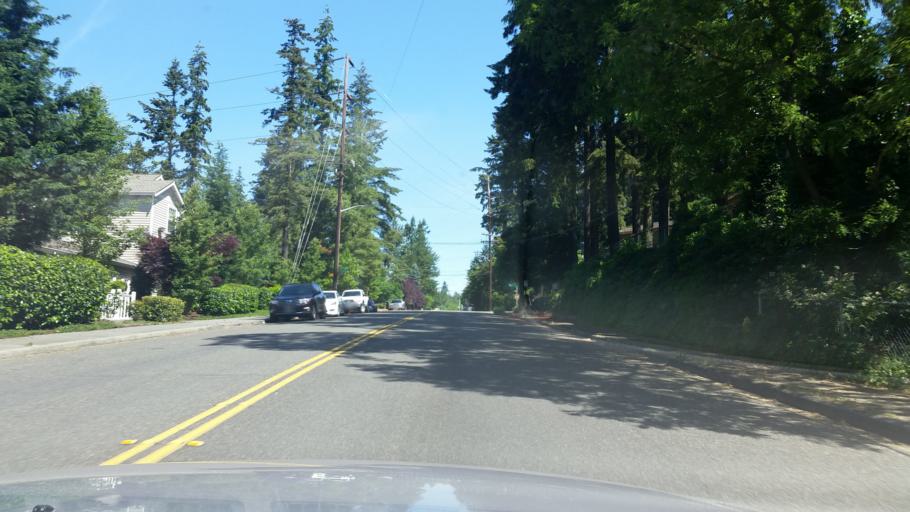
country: US
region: Washington
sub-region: Snohomish County
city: Mountlake Terrace
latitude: 47.7732
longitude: -122.3135
